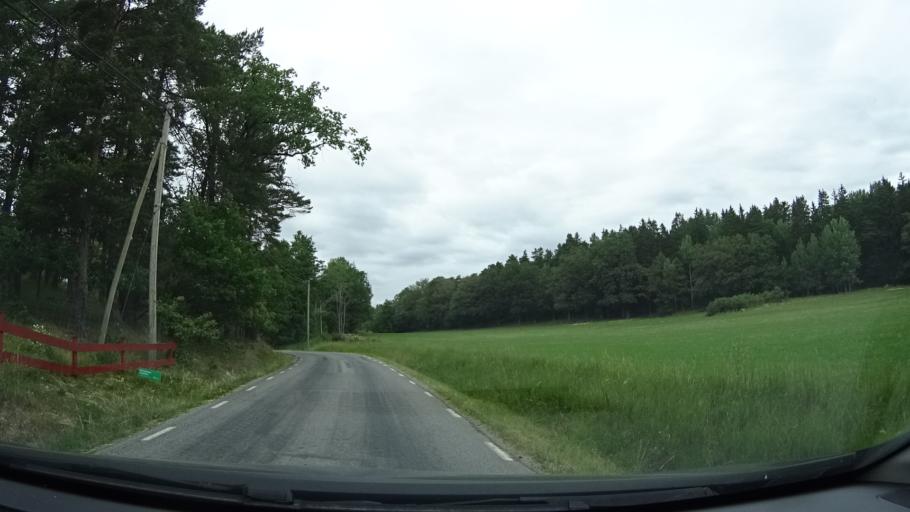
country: SE
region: Stockholm
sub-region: Varmdo Kommun
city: Mortnas
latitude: 59.3747
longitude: 18.4652
